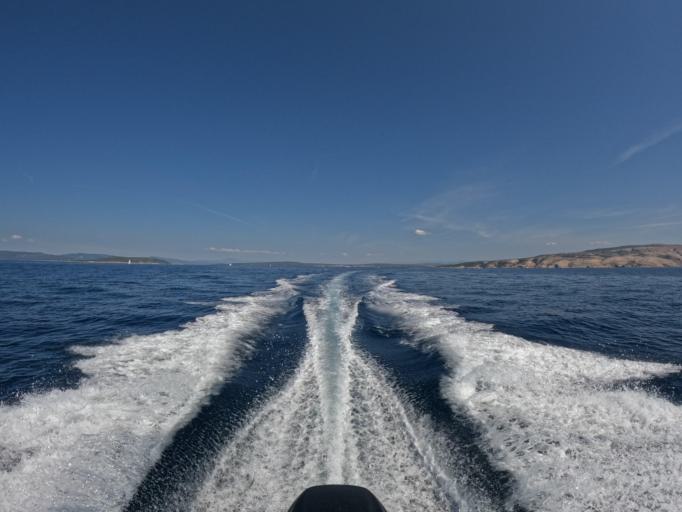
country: HR
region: Primorsko-Goranska
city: Punat
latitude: 44.9312
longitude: 14.6171
